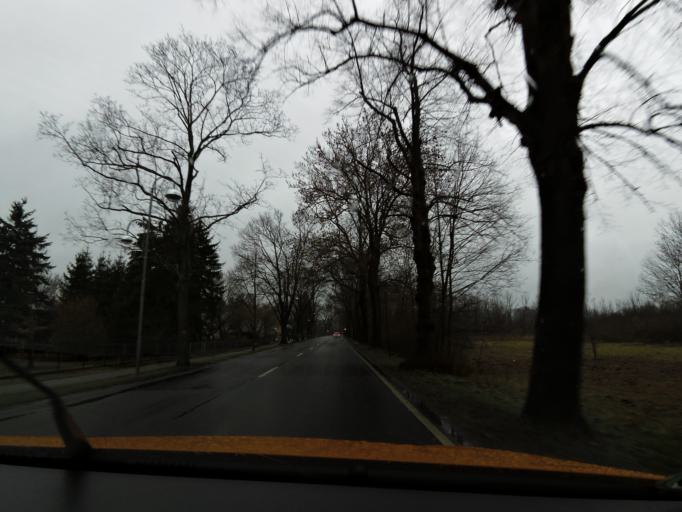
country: DE
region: Brandenburg
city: Zossen
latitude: 52.2531
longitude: 13.4488
